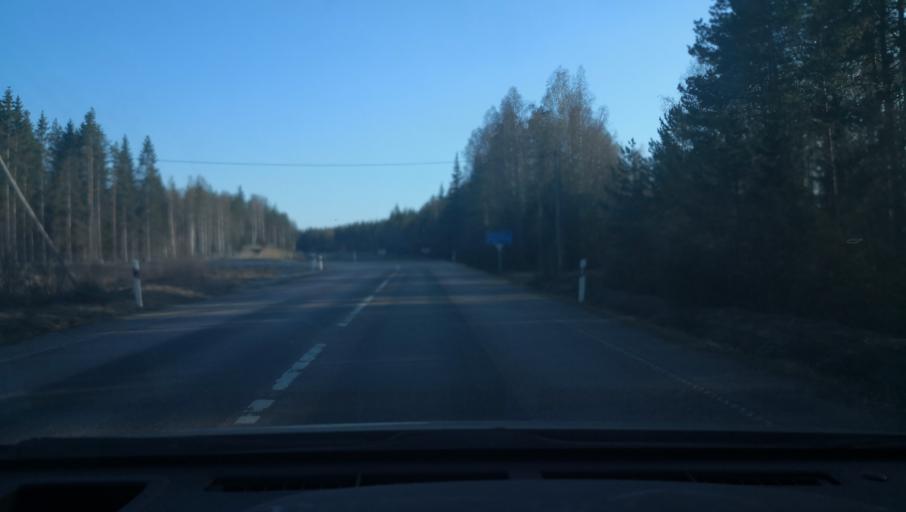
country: SE
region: Uppsala
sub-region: Heby Kommun
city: Heby
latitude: 59.9697
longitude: 16.8354
